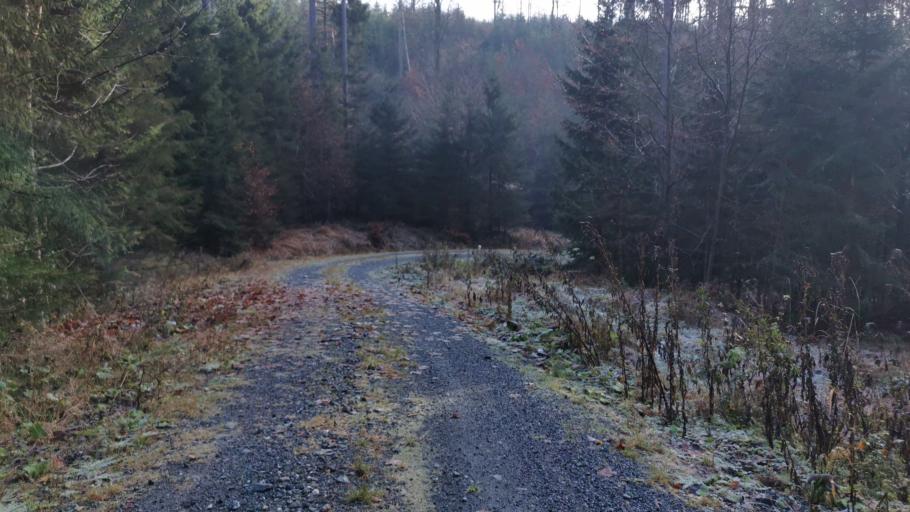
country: DE
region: Bavaria
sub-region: Upper Franconia
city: Tschirn
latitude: 50.4382
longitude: 11.4561
